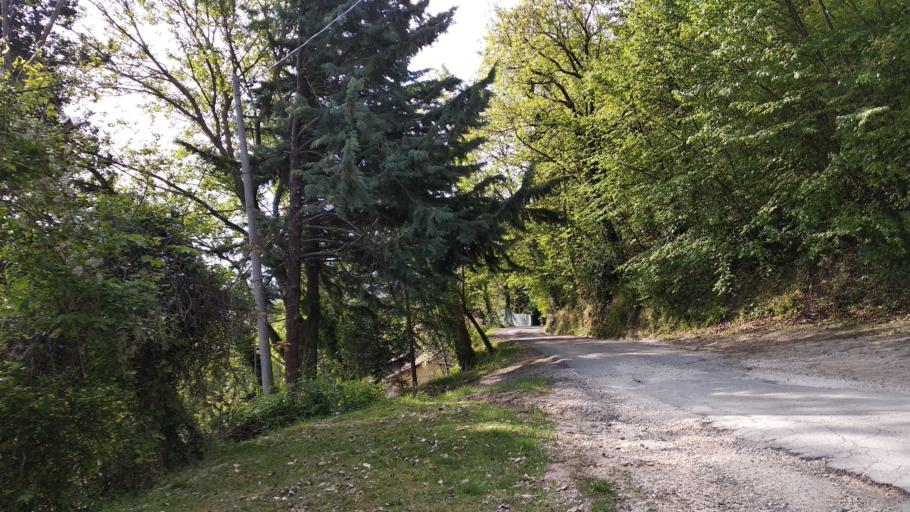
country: IT
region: Emilia-Romagna
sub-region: Provincia di Ravenna
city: Fognano
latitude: 44.2252
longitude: 11.7460
